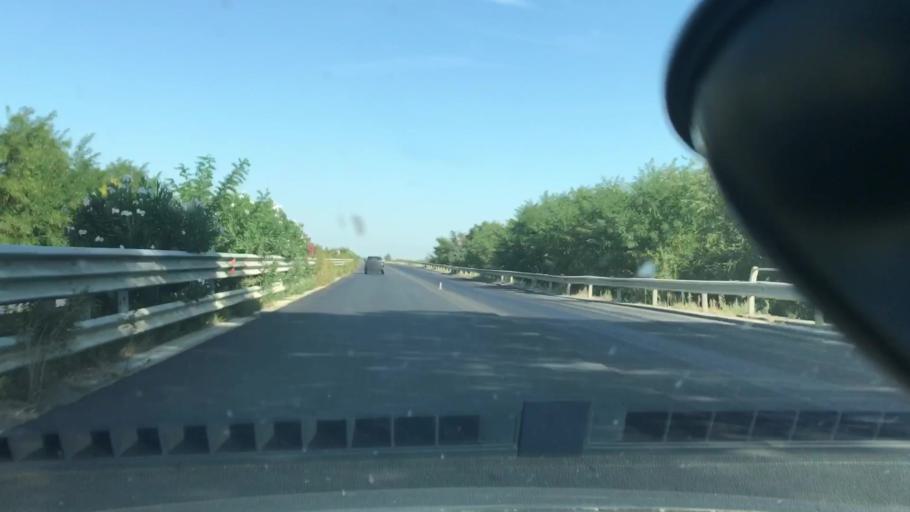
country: IT
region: Apulia
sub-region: Provincia di Foggia
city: Ascoli Satriano
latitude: 41.2744
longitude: 15.5533
